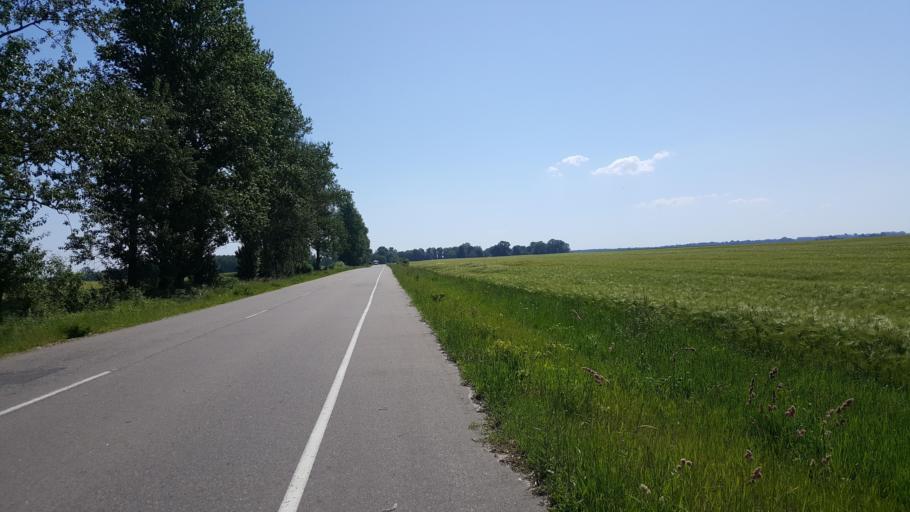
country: BY
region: Brest
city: Zhabinka
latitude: 52.2368
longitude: 23.9910
